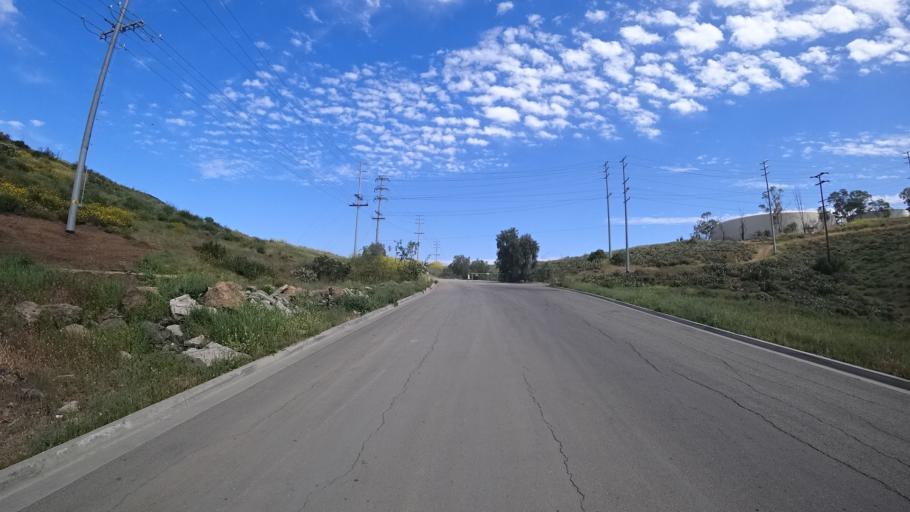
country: US
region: California
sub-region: Ventura County
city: Casa Conejo
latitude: 34.1966
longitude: -118.9384
